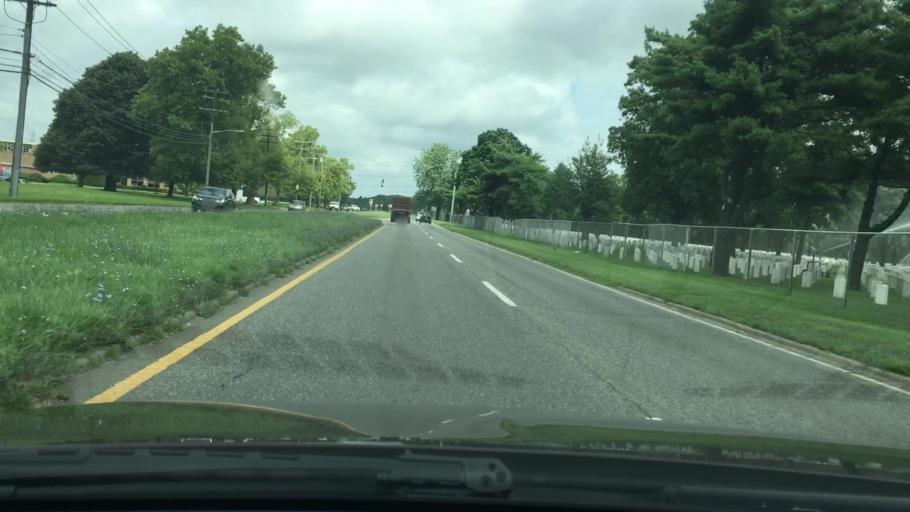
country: US
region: New York
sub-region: Suffolk County
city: Wheatley Heights
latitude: 40.7600
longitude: -73.4030
